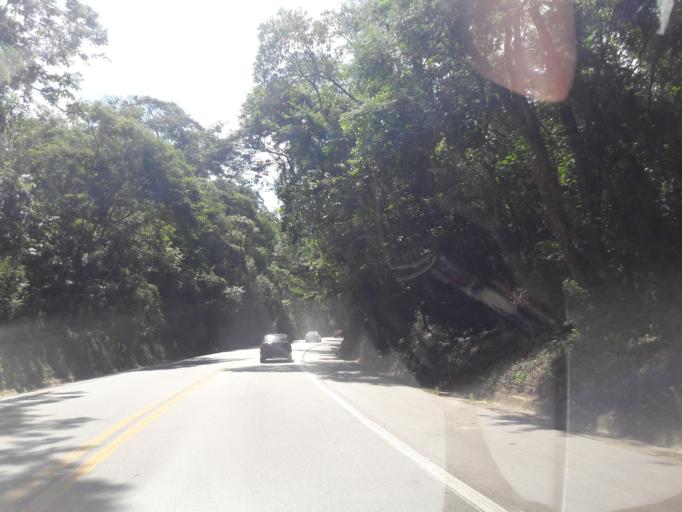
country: BR
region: Sao Paulo
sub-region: Francisco Morato
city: Francisco Morato
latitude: -23.2727
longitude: -46.7940
